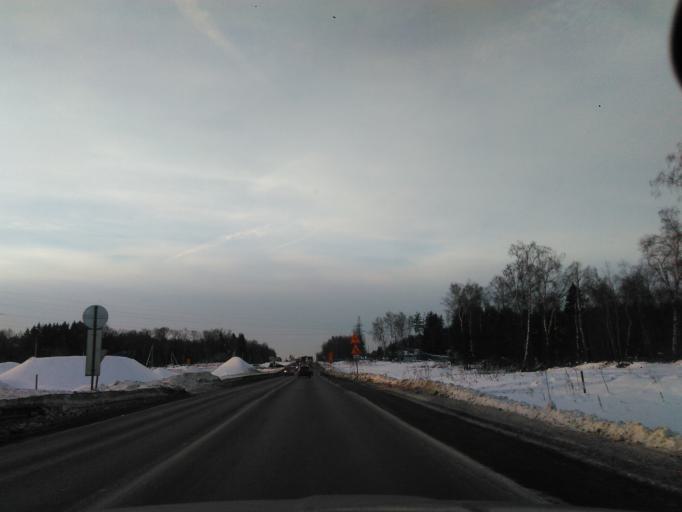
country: RU
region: Moskovskaya
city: Istra
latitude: 55.9206
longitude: 36.9460
